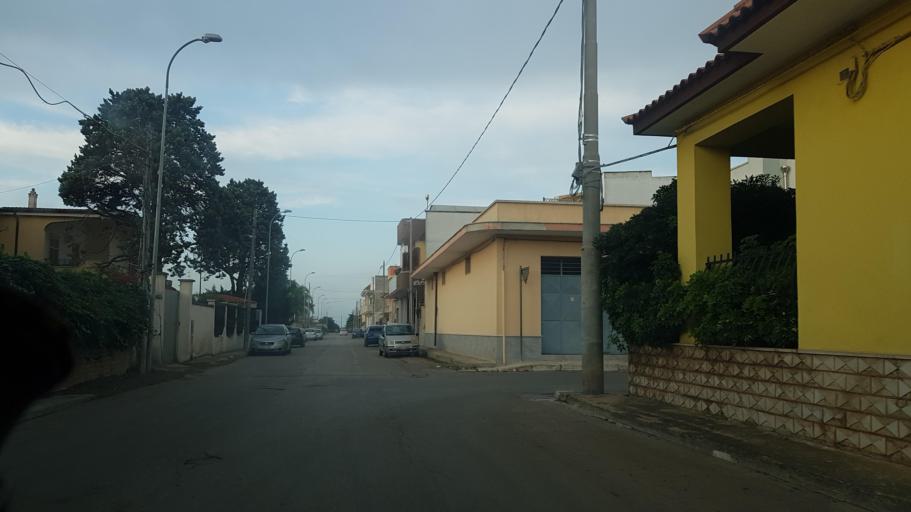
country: IT
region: Apulia
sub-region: Provincia di Brindisi
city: San Pancrazio Salentino
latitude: 40.4188
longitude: 17.8294
